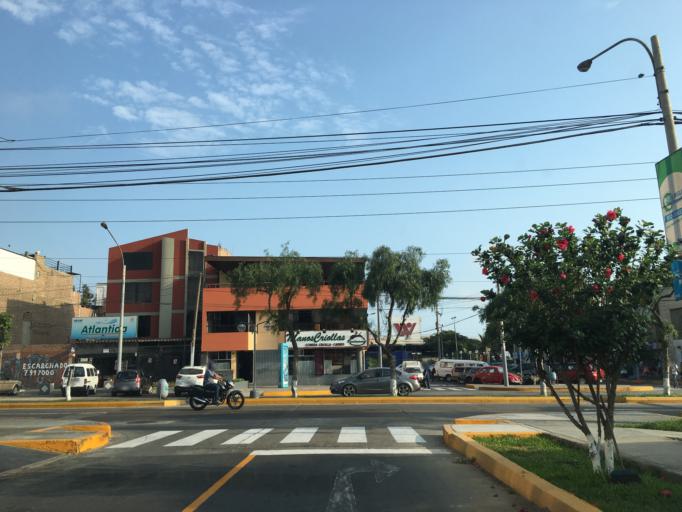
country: PE
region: Callao
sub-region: Callao
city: Callao
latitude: -12.0746
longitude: -77.0813
